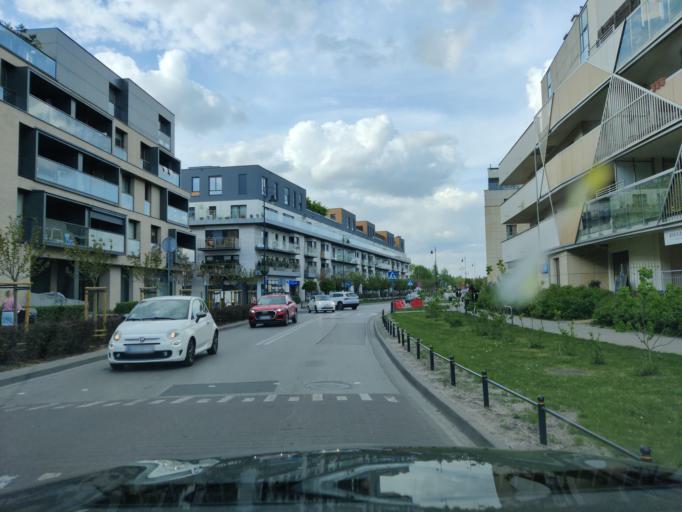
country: PL
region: Masovian Voivodeship
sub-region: Warszawa
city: Wilanow
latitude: 52.1660
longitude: 21.0746
